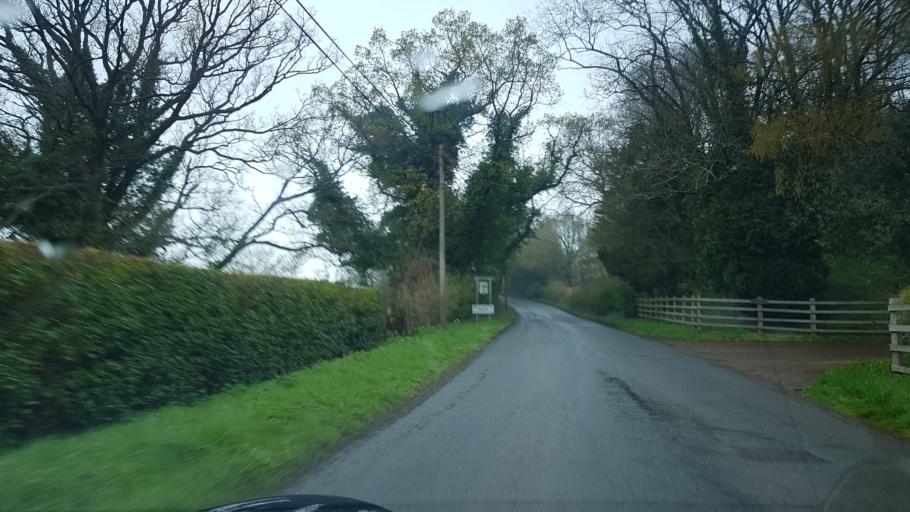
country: GB
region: England
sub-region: Herefordshire
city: Ledbury
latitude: 52.0548
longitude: -2.4247
